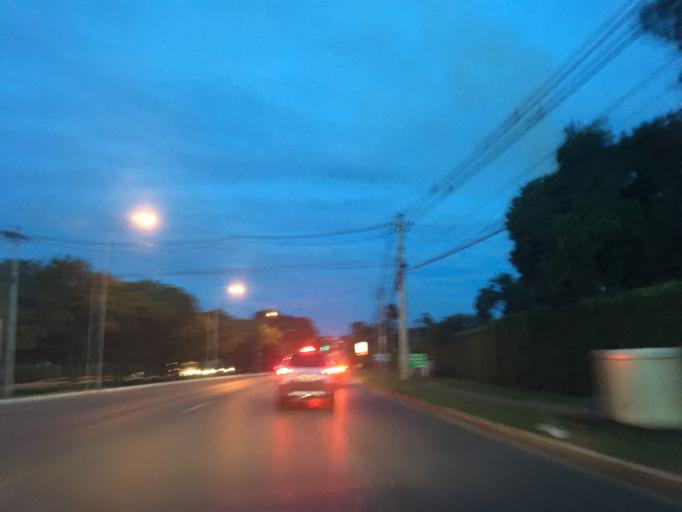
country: BR
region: Federal District
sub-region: Brasilia
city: Brasilia
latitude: -15.8438
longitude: -47.8518
